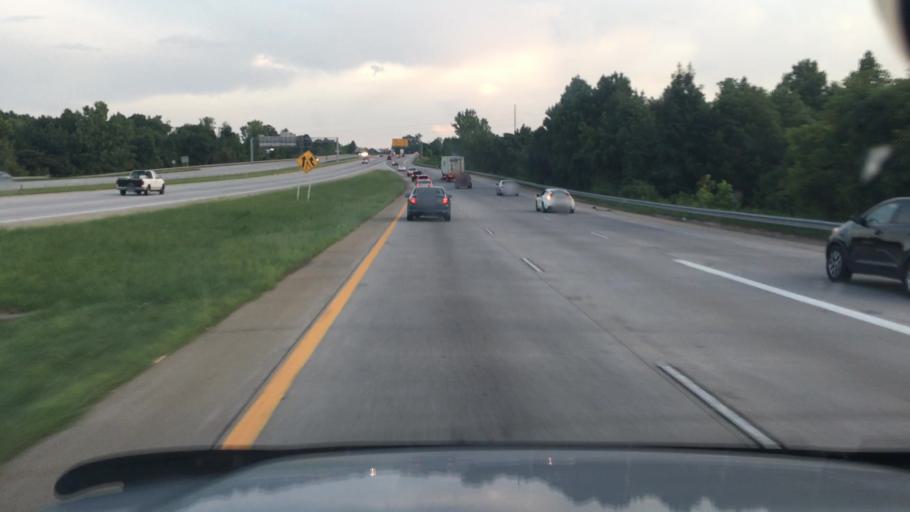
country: US
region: North Carolina
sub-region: Gaston County
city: Belmont
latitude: 35.2346
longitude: -80.9706
